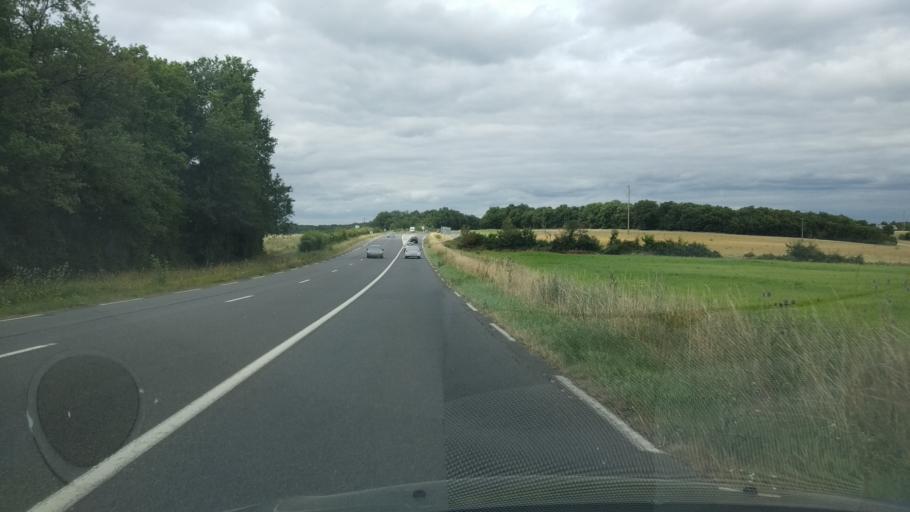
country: FR
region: Poitou-Charentes
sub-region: Departement de la Vienne
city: Smarves
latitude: 46.5284
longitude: 0.3537
